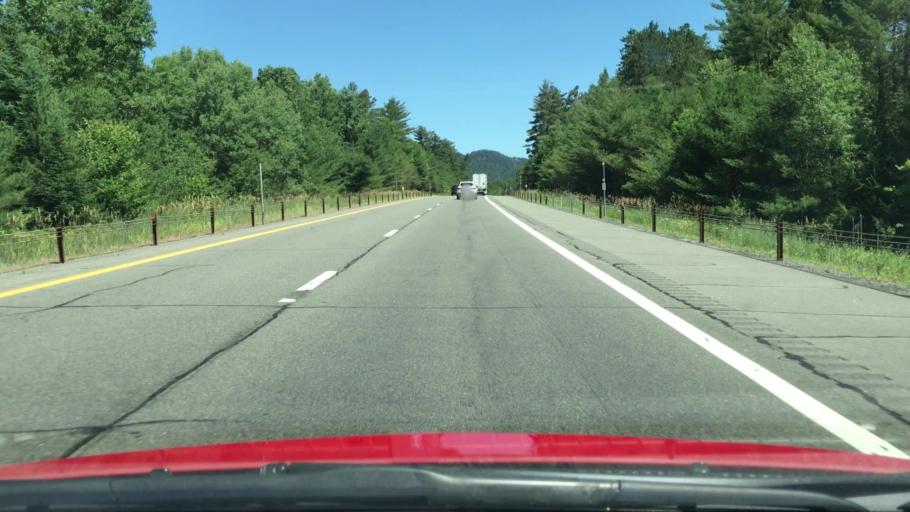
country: US
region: New York
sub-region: Essex County
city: Mineville
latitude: 43.9754
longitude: -73.7248
